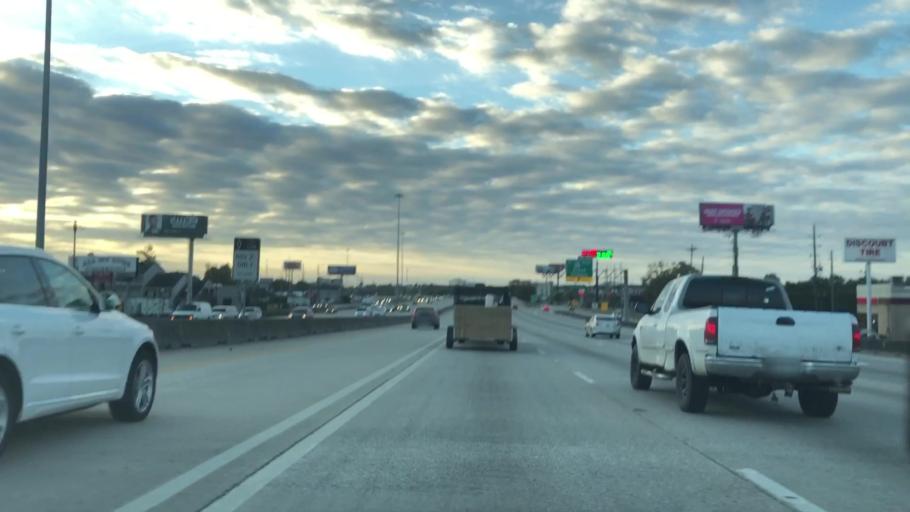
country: US
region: Texas
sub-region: Montgomery County
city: Oak Ridge North
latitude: 30.1245
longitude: -95.4428
